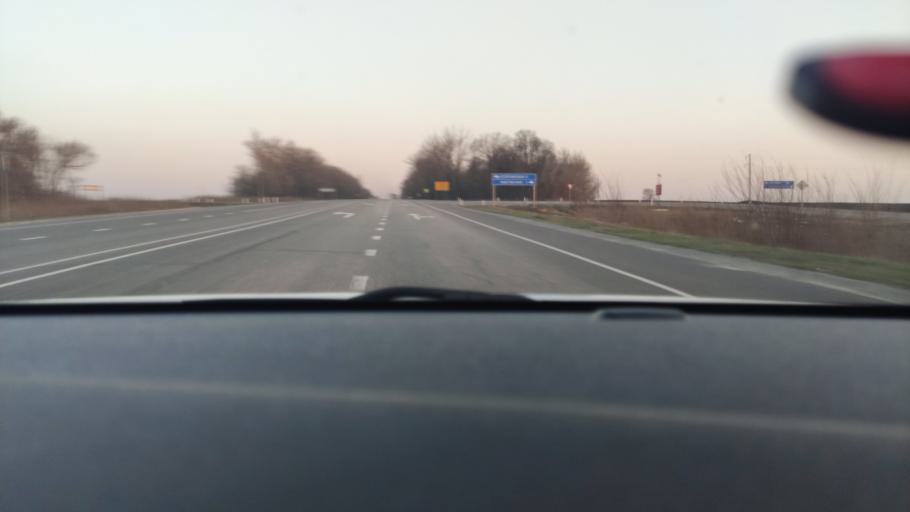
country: RU
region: Voronezj
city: Uryv-Pokrovka
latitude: 51.2027
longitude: 39.0790
